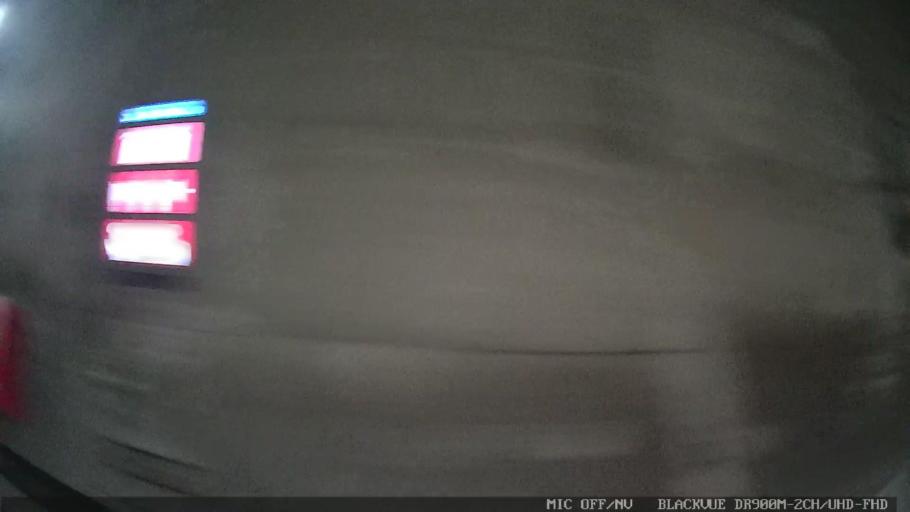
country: BR
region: Sao Paulo
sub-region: Cubatao
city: Cubatao
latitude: -23.9137
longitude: -46.5279
